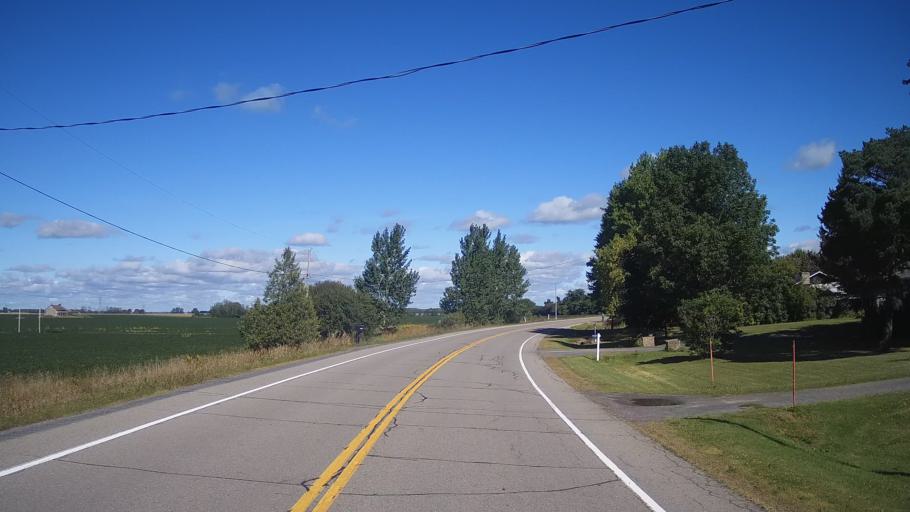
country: US
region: New York
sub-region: St. Lawrence County
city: Norfolk
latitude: 44.9577
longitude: -75.2824
